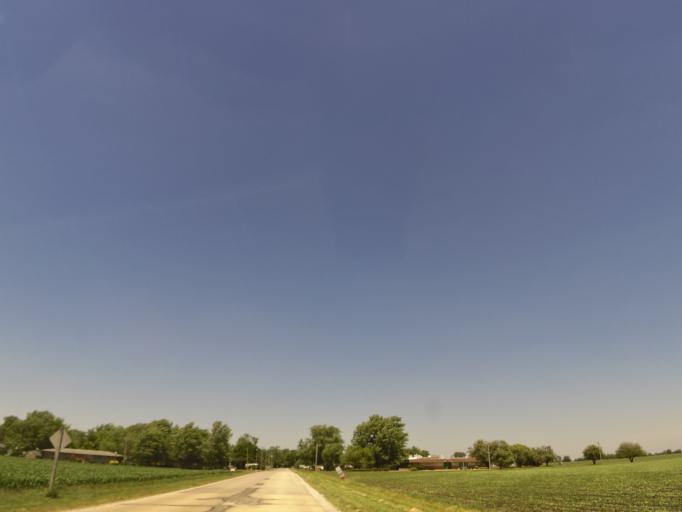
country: US
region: Illinois
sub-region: Livingston County
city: Chatsworth
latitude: 40.7506
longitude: -88.1826
